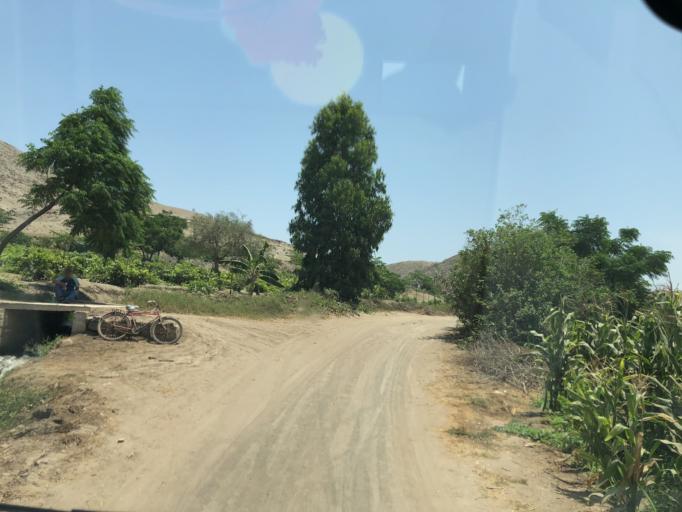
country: PE
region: Lima
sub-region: Provincia de Canete
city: Quilmana
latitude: -12.9923
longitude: -76.4387
